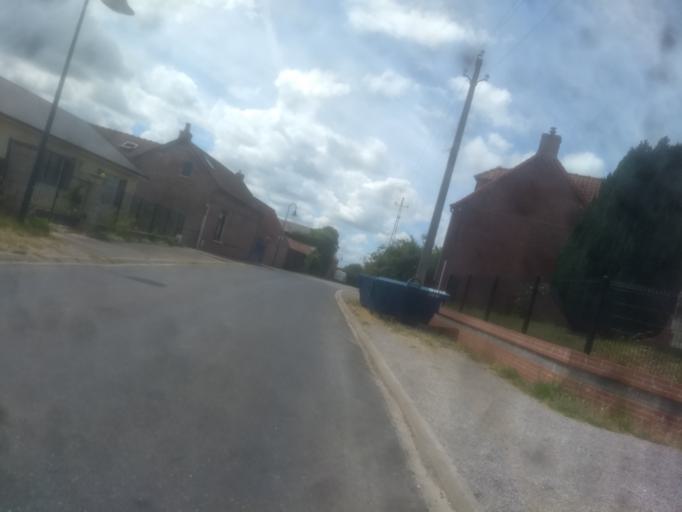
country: FR
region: Nord-Pas-de-Calais
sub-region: Departement du Pas-de-Calais
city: Mont-Saint-Eloi
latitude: 50.3450
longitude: 2.6715
